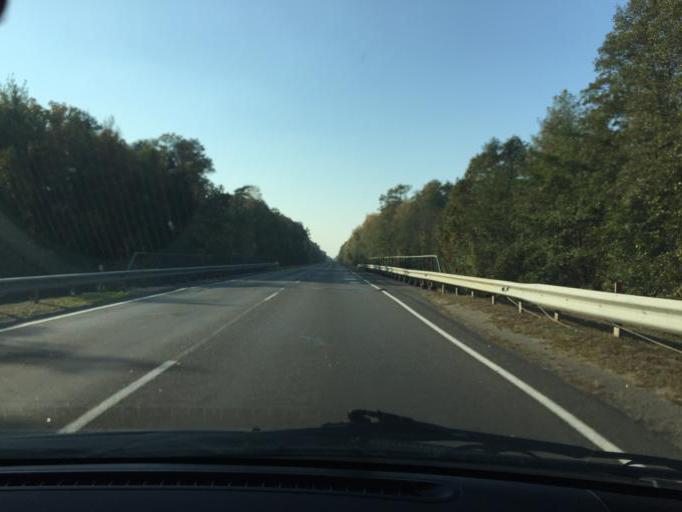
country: BY
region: Brest
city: Mikashevichy
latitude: 52.2417
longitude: 27.4758
